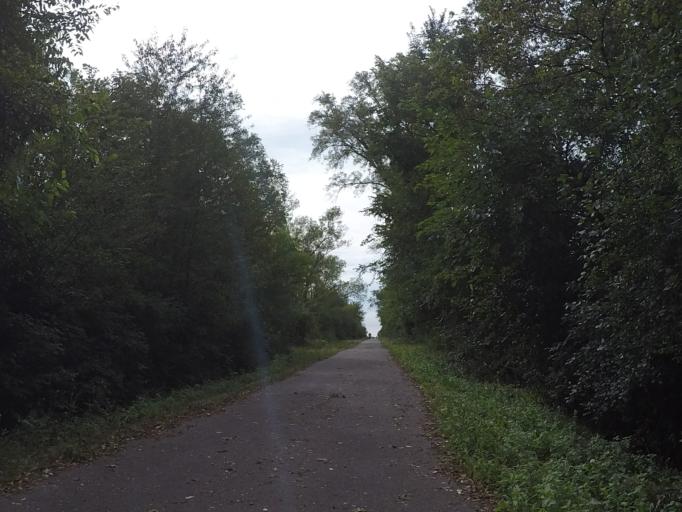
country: US
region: Wisconsin
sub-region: Sauk County
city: Prairie du Sac
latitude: 43.3279
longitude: -89.7485
